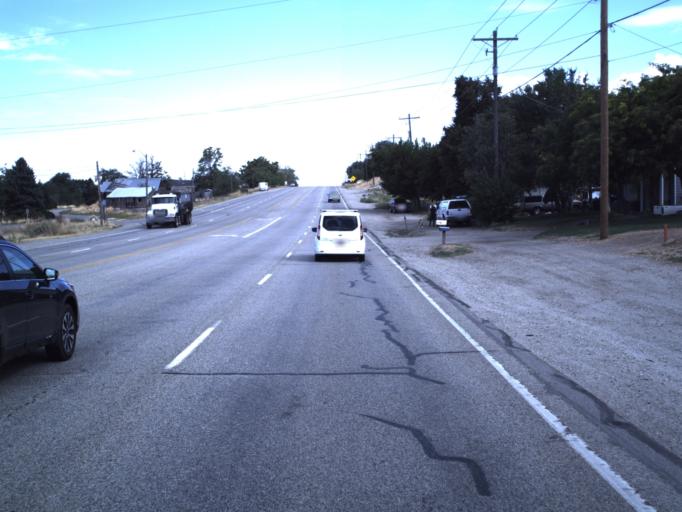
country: US
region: Utah
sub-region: Box Elder County
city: Willard
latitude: 41.4342
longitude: -112.0357
